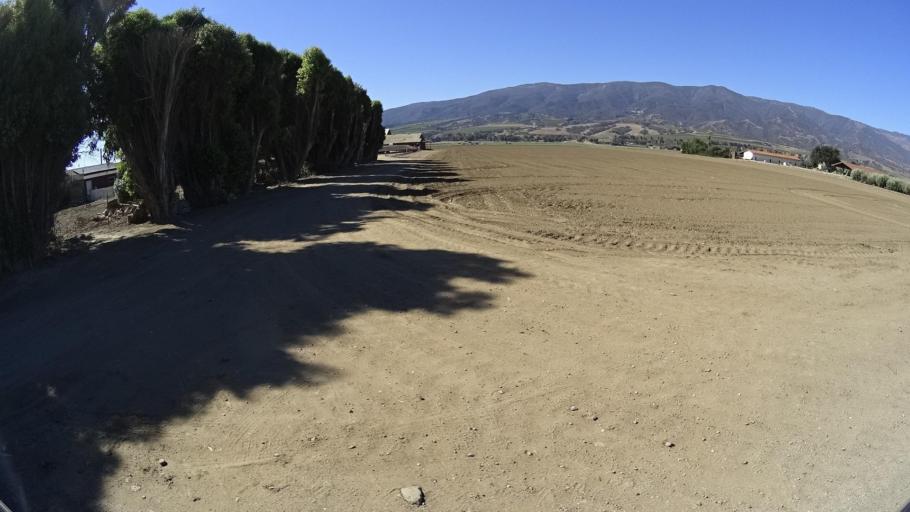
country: US
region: California
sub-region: Monterey County
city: Soledad
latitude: 36.4063
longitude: -121.3529
